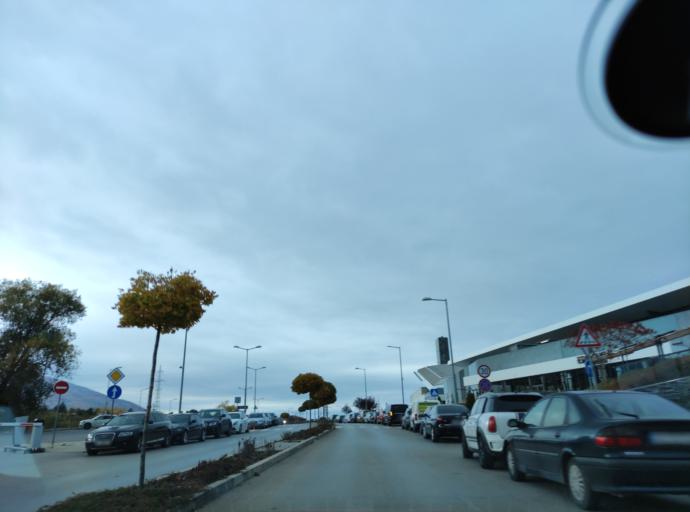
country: BG
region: Sofia-Capital
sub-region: Stolichna Obshtina
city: Sofia
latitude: 42.6233
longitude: 23.3527
